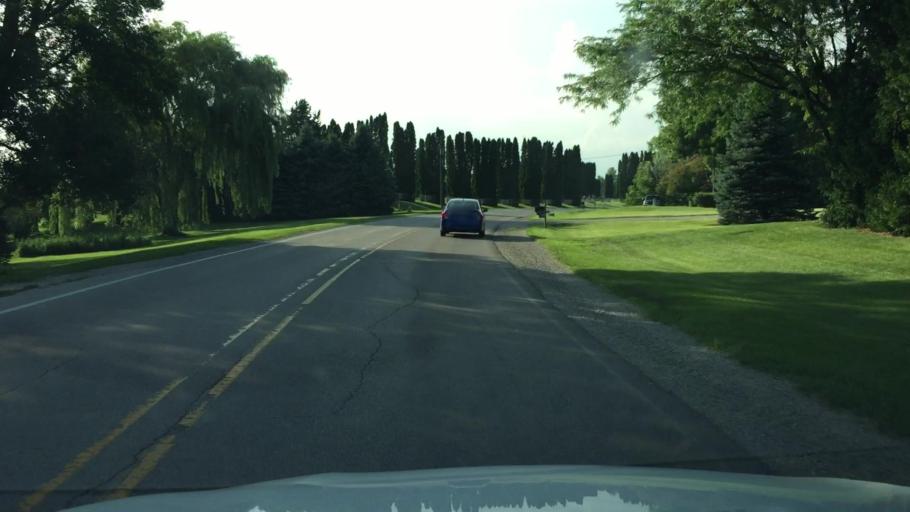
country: US
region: Iowa
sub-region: Linn County
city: Ely
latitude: 41.8420
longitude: -91.6454
